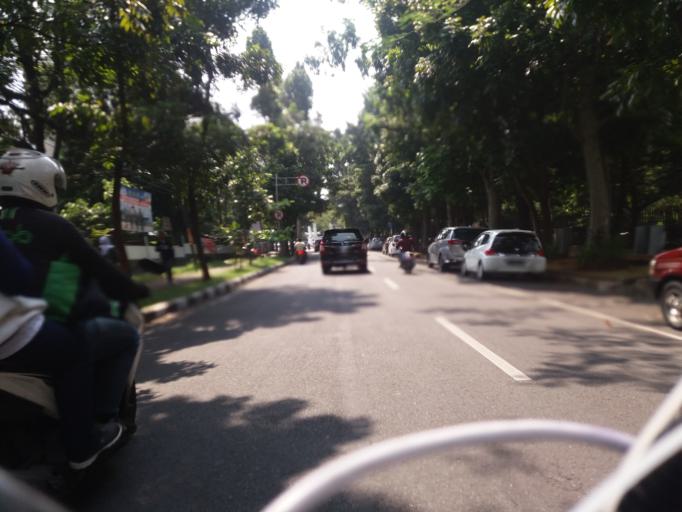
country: ID
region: West Java
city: Bandung
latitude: -6.9109
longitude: 107.6125
